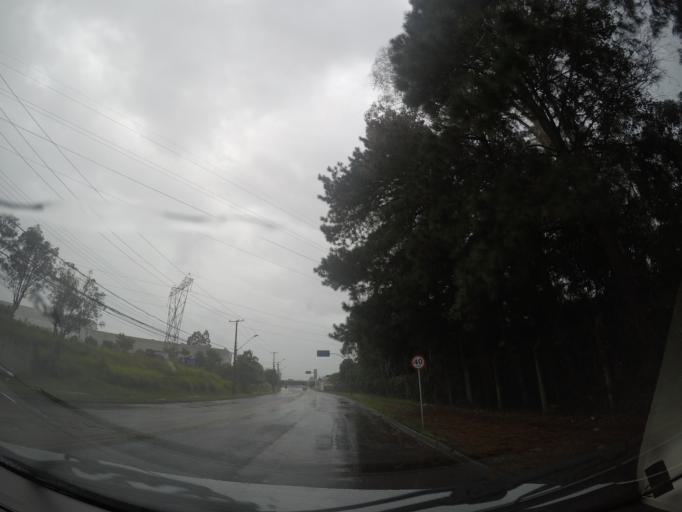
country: BR
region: Parana
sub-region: Curitiba
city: Curitiba
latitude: -25.4513
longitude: -49.3596
